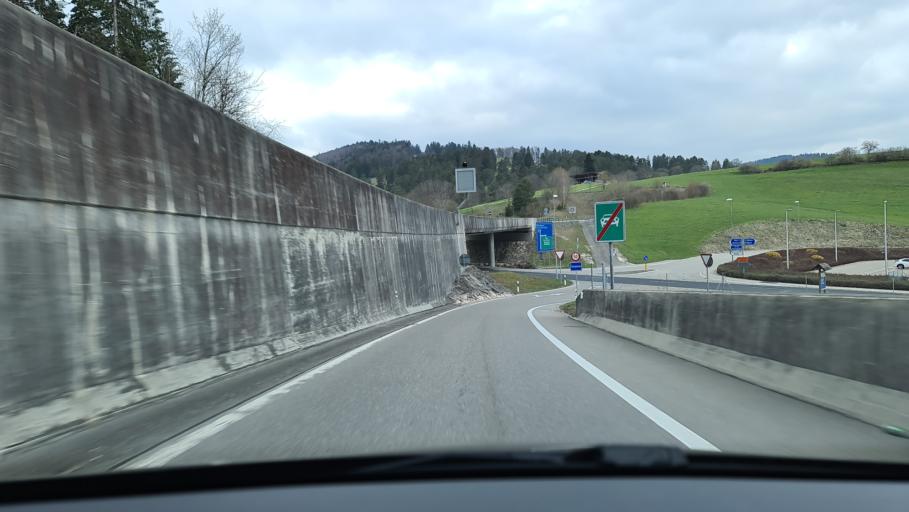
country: CH
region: Bern
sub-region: Jura bernois
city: Tavannes
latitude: 47.2145
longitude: 7.1930
